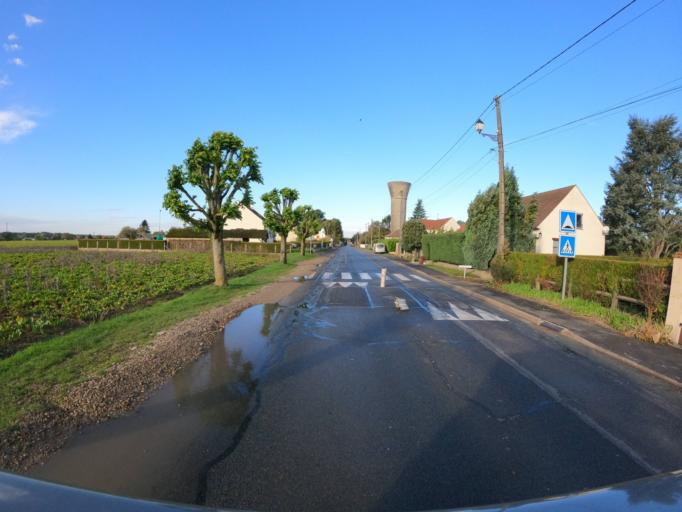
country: FR
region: Ile-de-France
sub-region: Departement de Seine-et-Marne
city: Serris
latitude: 48.8378
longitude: 2.7603
